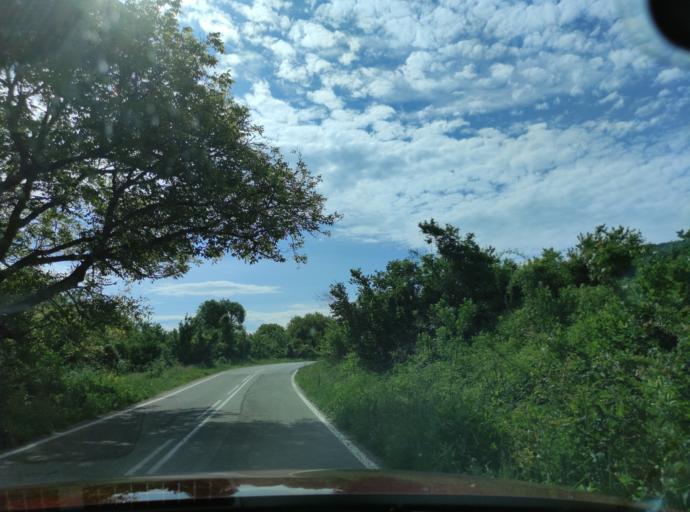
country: BG
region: Montana
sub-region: Obshtina Chiprovtsi
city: Chiprovtsi
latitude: 43.4857
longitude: 22.8176
